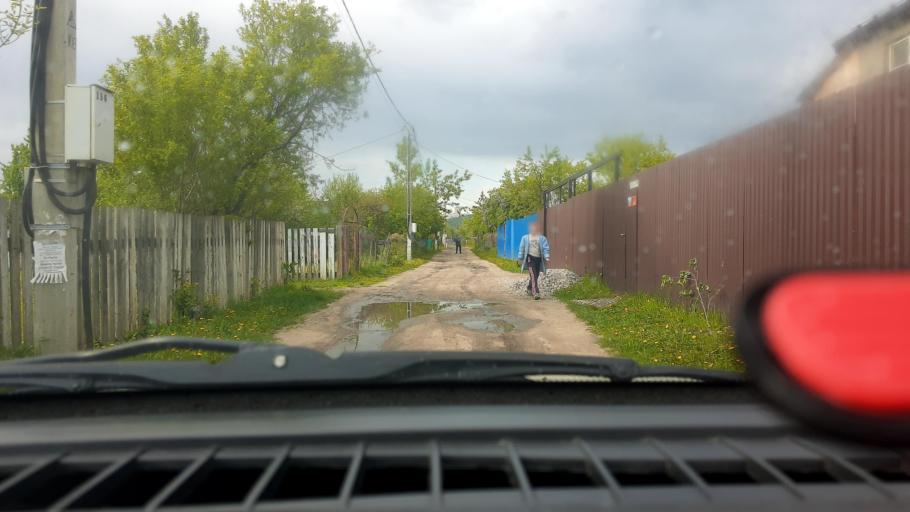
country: RU
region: Nizjnij Novgorod
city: Nizhniy Novgorod
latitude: 56.2672
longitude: 43.9542
